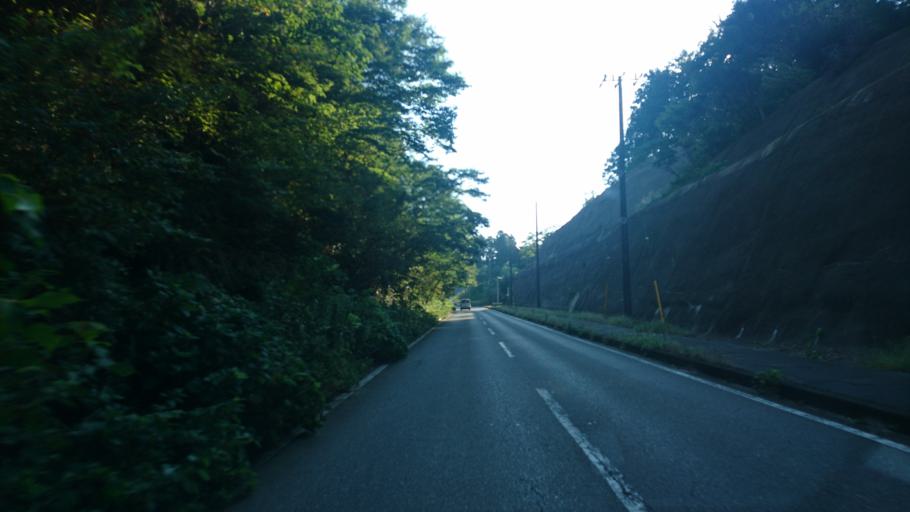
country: JP
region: Chiba
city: Kawaguchi
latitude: 35.2078
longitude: 140.0240
